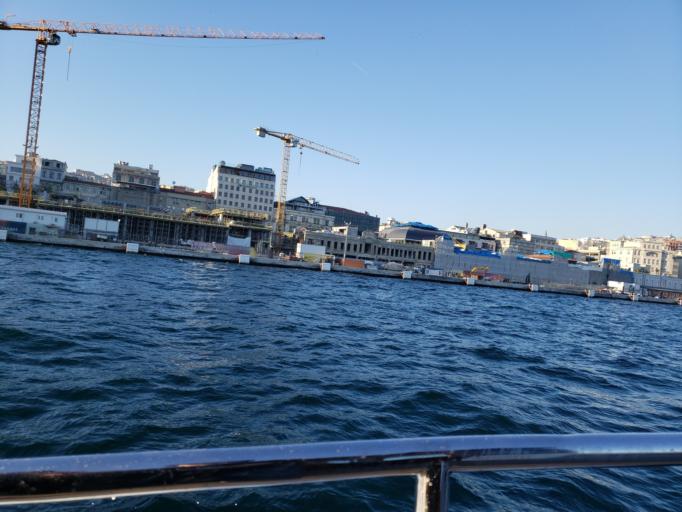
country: TR
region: Istanbul
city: Eminoenue
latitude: 41.0224
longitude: 28.9803
